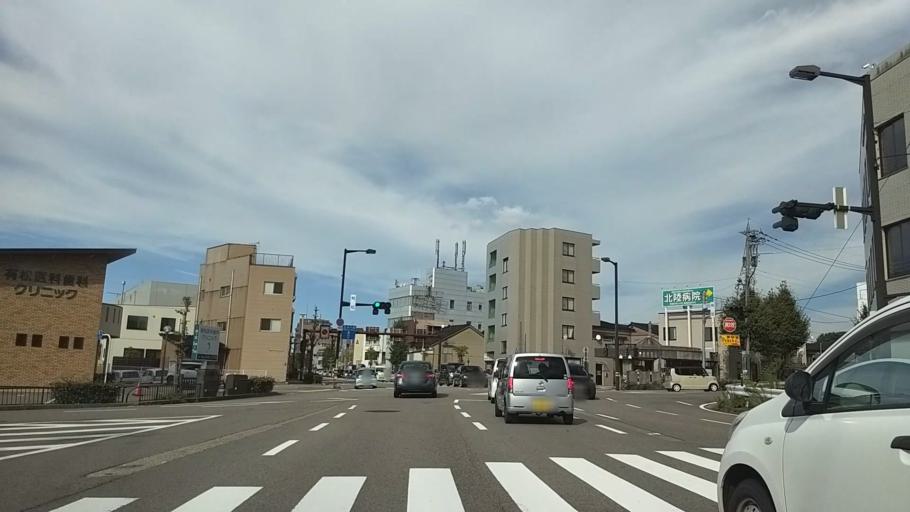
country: JP
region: Ishikawa
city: Nonoichi
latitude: 36.5442
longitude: 136.6411
